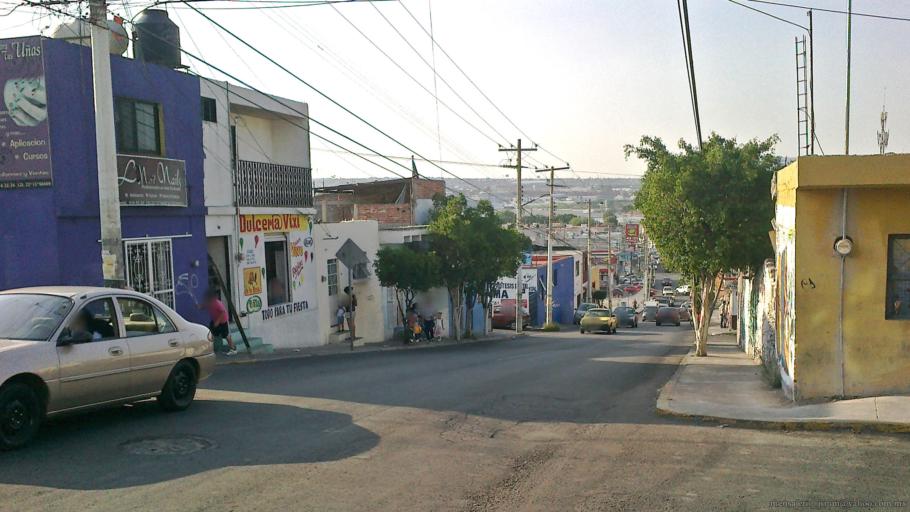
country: MX
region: Queretaro
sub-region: Queretaro
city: Santiago de Queretaro
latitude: 20.6081
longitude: -100.3994
